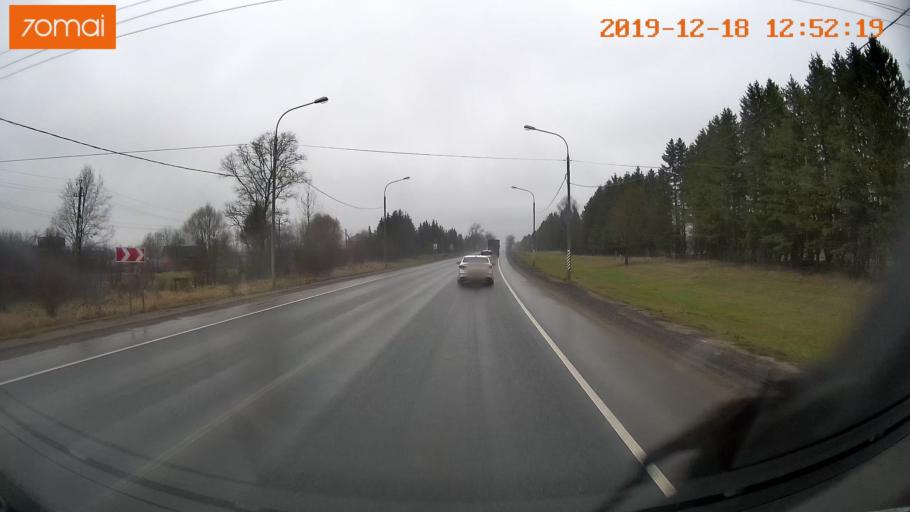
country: RU
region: Moskovskaya
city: Klin
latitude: 56.3104
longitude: 36.6868
